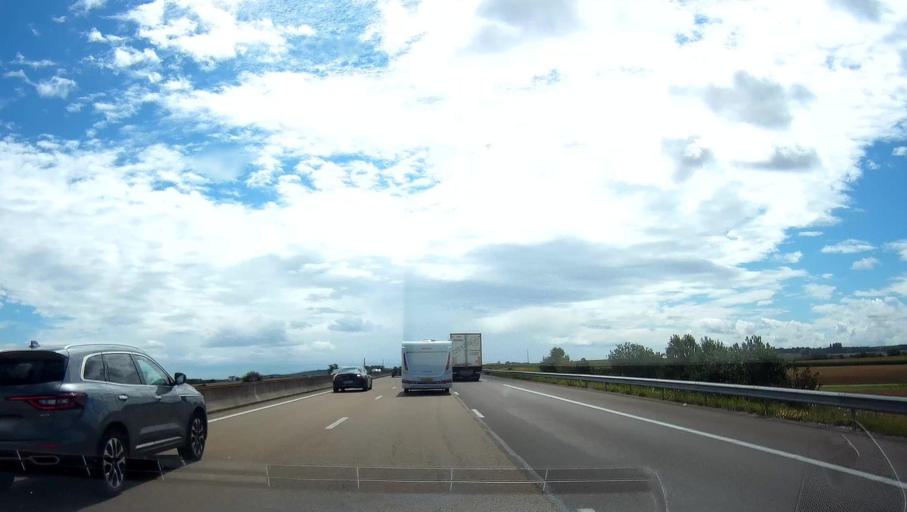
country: FR
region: Bourgogne
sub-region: Departement de la Cote-d'Or
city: Marcilly-sur-Tille
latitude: 47.5056
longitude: 5.1930
